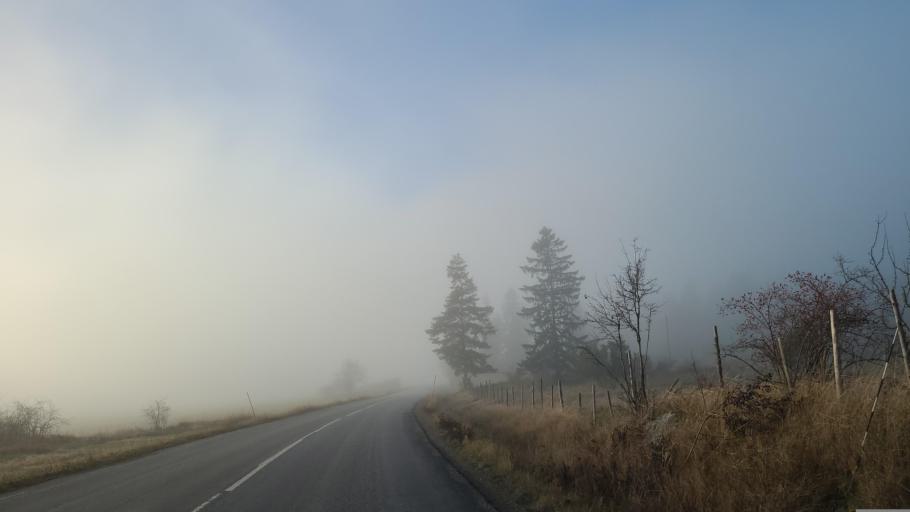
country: SE
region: Uppsala
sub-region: Enkopings Kommun
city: Grillby
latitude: 59.5936
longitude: 17.2231
